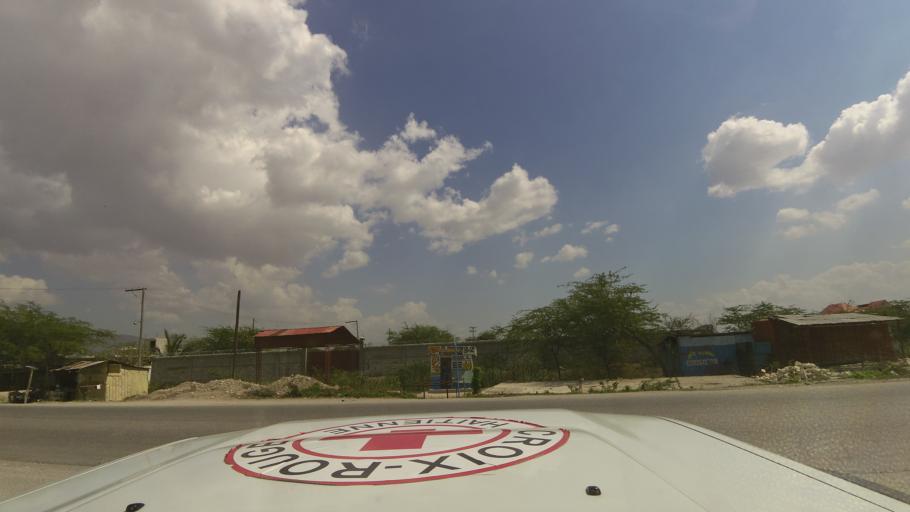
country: HT
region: Ouest
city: Croix des Bouquets
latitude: 18.6419
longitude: -72.2621
